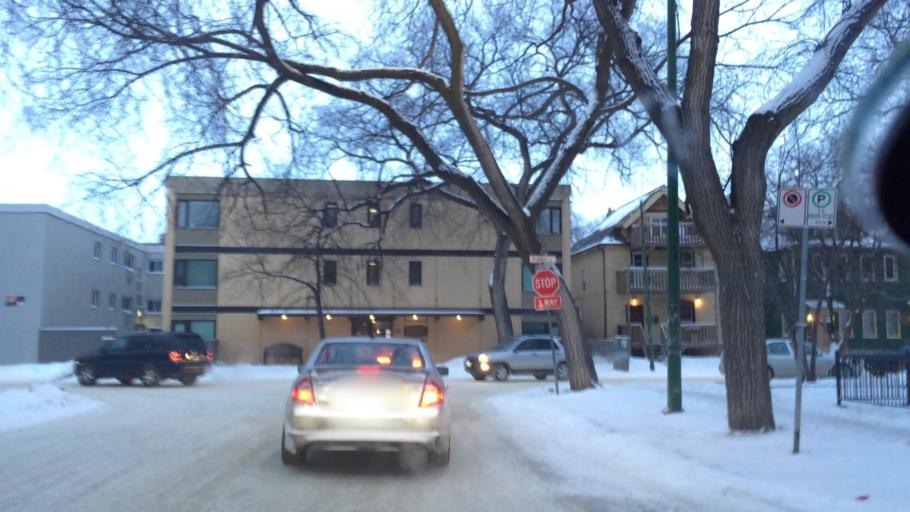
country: CA
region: Manitoba
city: Winnipeg
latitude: 49.8802
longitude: -97.1587
